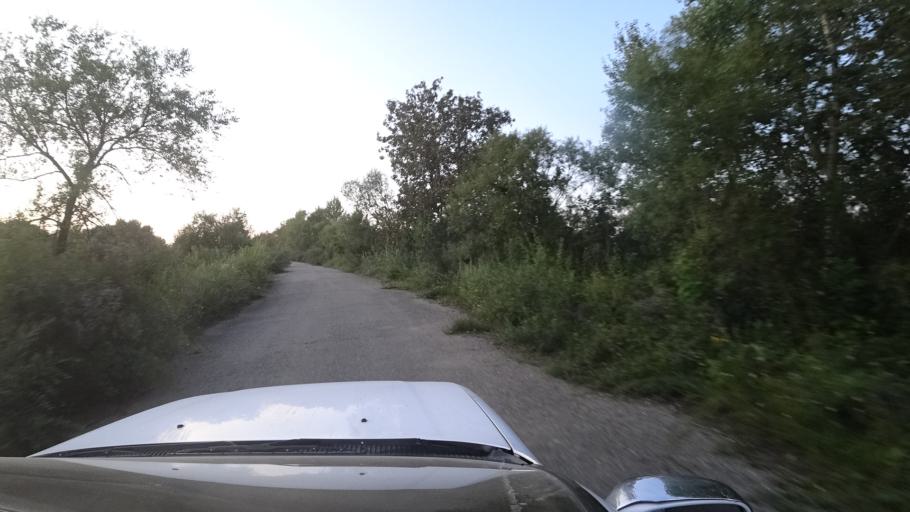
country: RU
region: Primorskiy
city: Dal'nerechensk
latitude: 45.9459
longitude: 133.7645
